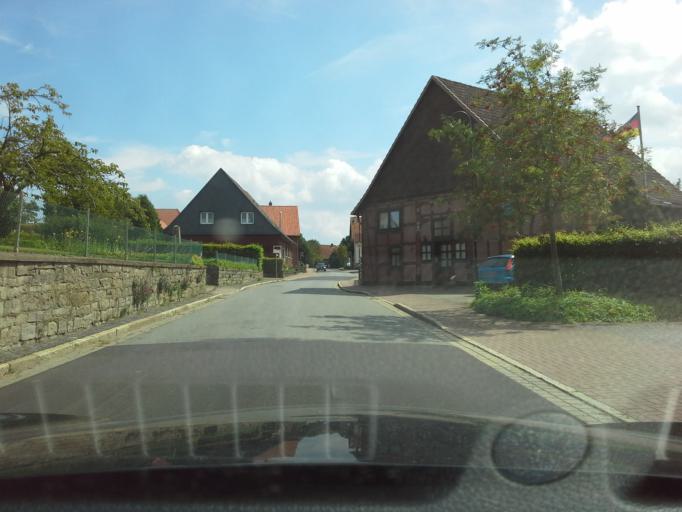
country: DE
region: Lower Saxony
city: Messenkamp
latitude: 52.2598
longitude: 9.3821
